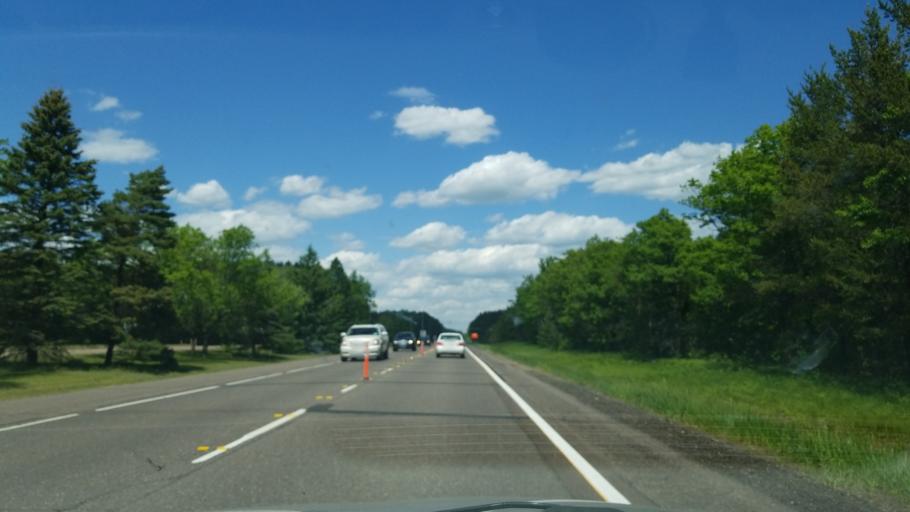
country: US
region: Minnesota
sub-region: Carlton County
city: Moose Lake
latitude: 46.3568
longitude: -92.8048
